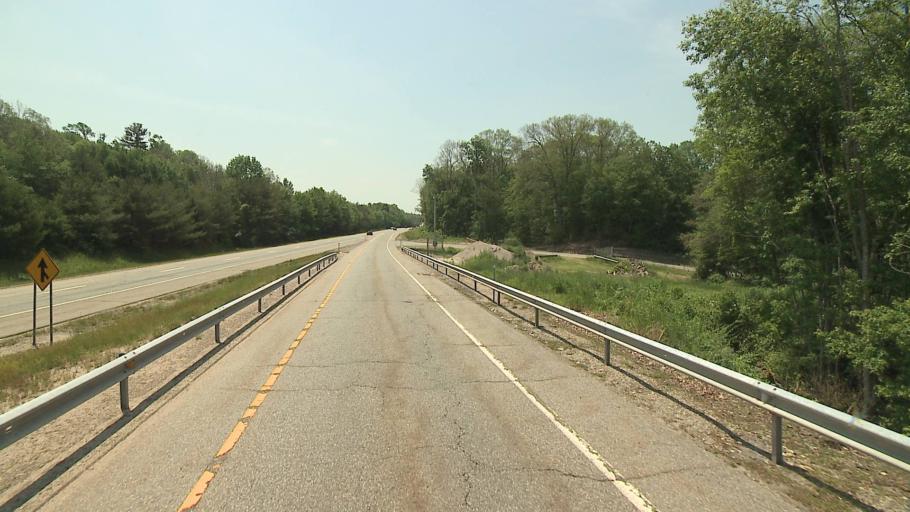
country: US
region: Connecticut
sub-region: Windham County
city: Thompson
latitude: 41.9649
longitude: -71.8738
